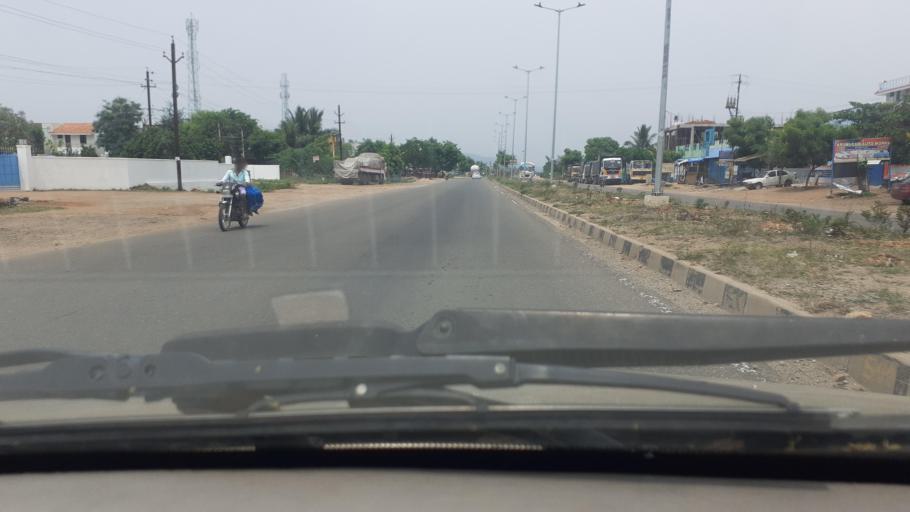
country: IN
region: Tamil Nadu
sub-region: Tirunelveli Kattabo
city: Tirunelveli
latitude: 8.7139
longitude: 77.7858
